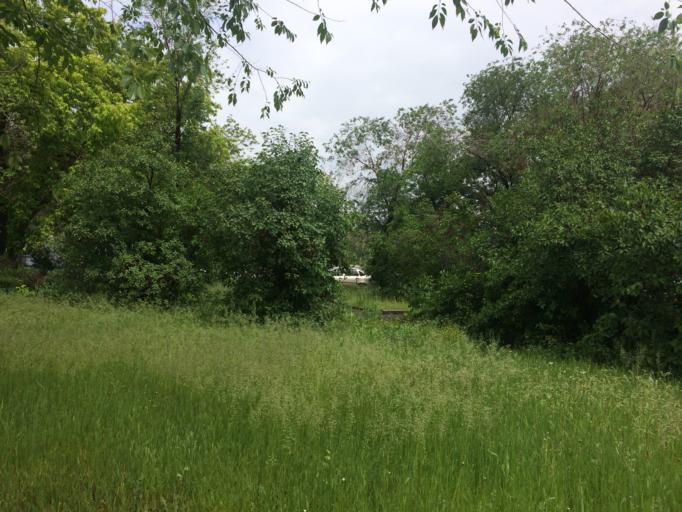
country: RU
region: Chelyabinsk
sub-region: Gorod Magnitogorsk
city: Magnitogorsk
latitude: 53.4136
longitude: 59.0560
